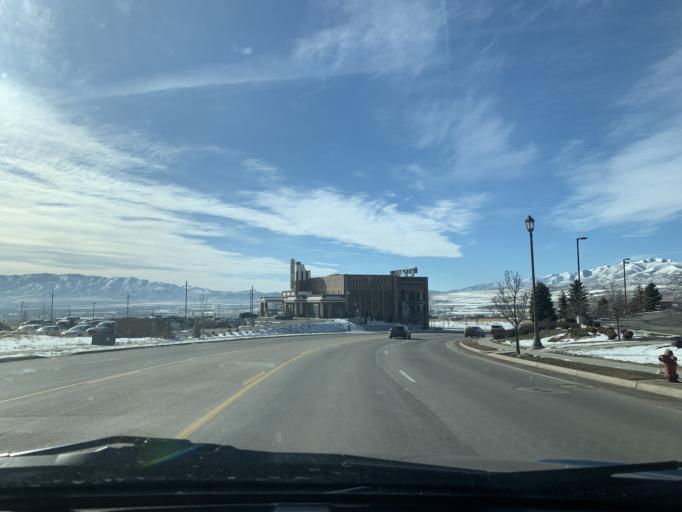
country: US
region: Utah
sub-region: Utah County
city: Lehi
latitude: 40.4337
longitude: -111.8832
